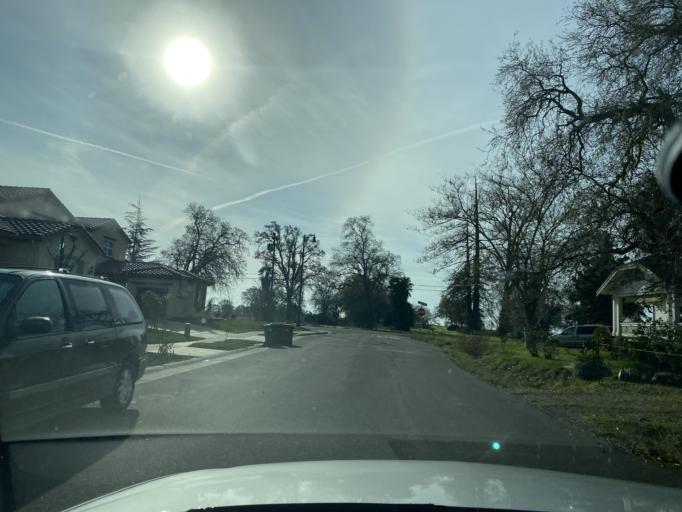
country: US
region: California
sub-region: Sacramento County
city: Elk Grove
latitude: 38.3914
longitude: -121.3878
